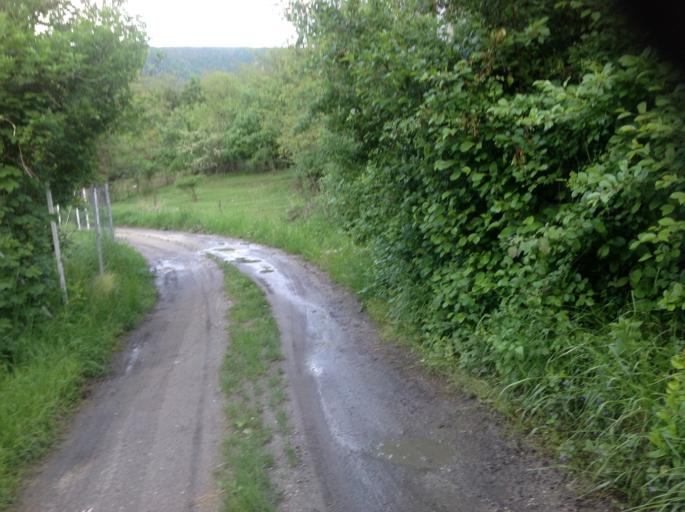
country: HU
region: Komarom-Esztergom
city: Kesztolc
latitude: 47.7110
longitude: 18.8020
